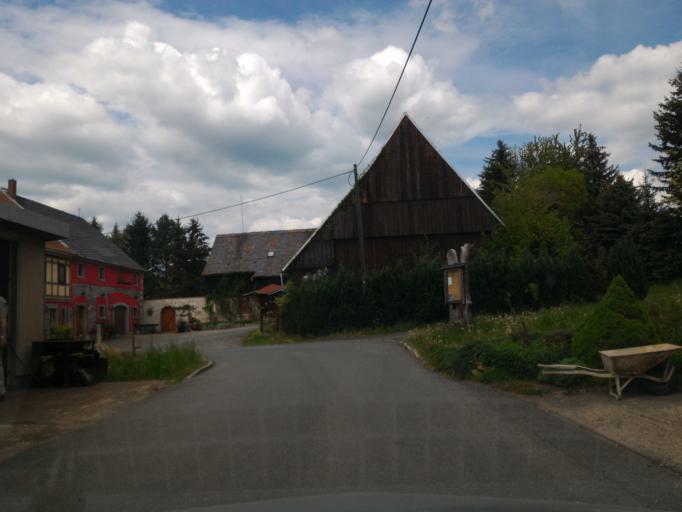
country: DE
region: Saxony
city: Seifhennersdorf
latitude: 50.9446
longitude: 14.6240
